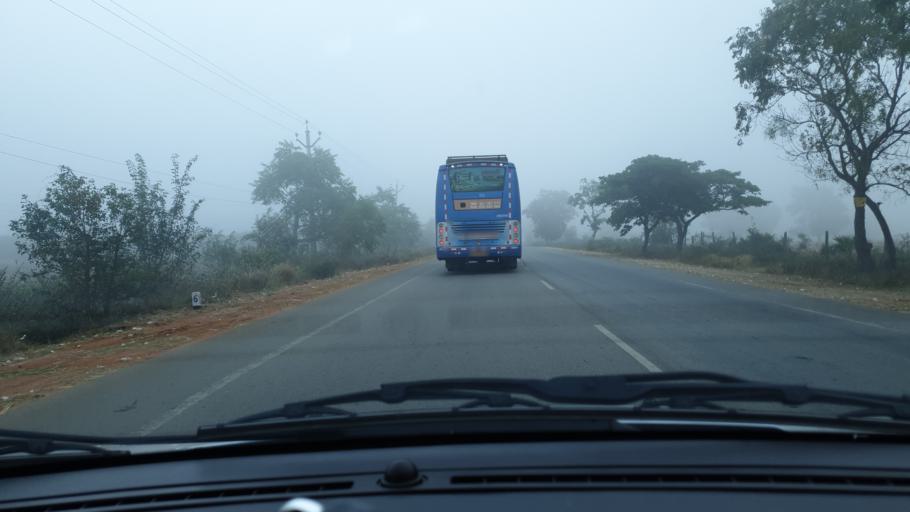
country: IN
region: Telangana
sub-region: Mahbubnagar
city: Nagar Karnul
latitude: 16.6640
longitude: 78.5444
